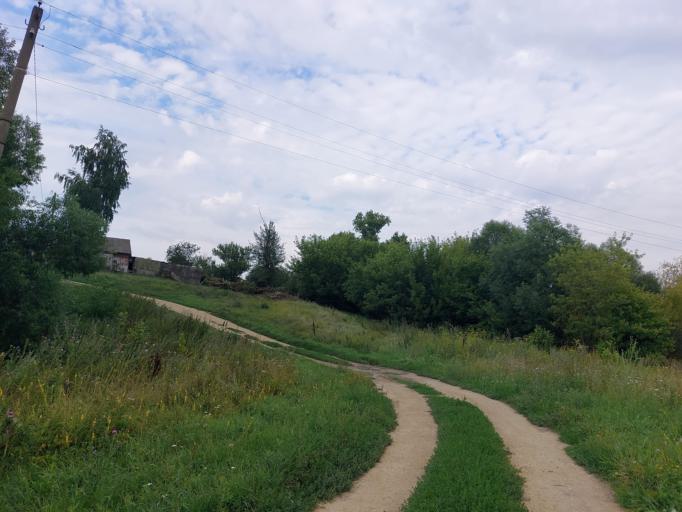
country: RU
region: Lipetsk
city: Dolgorukovo
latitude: 52.2882
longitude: 38.1874
